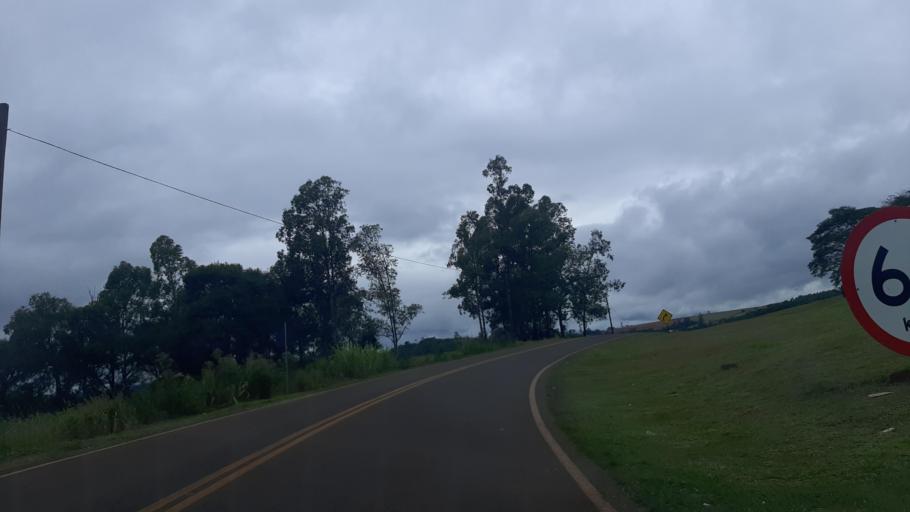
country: BR
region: Parana
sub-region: Ampere
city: Ampere
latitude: -25.9264
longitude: -53.4674
